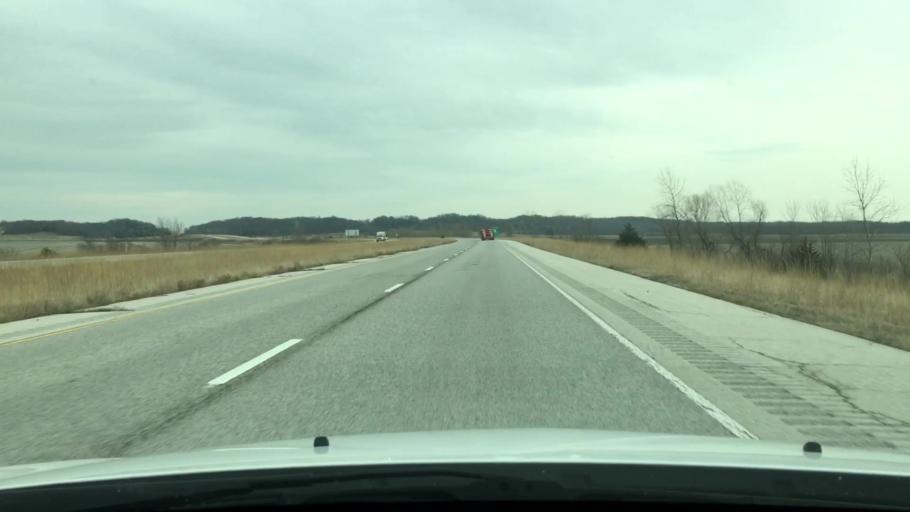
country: US
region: Illinois
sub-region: Pike County
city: Griggsville
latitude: 39.6869
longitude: -90.5934
